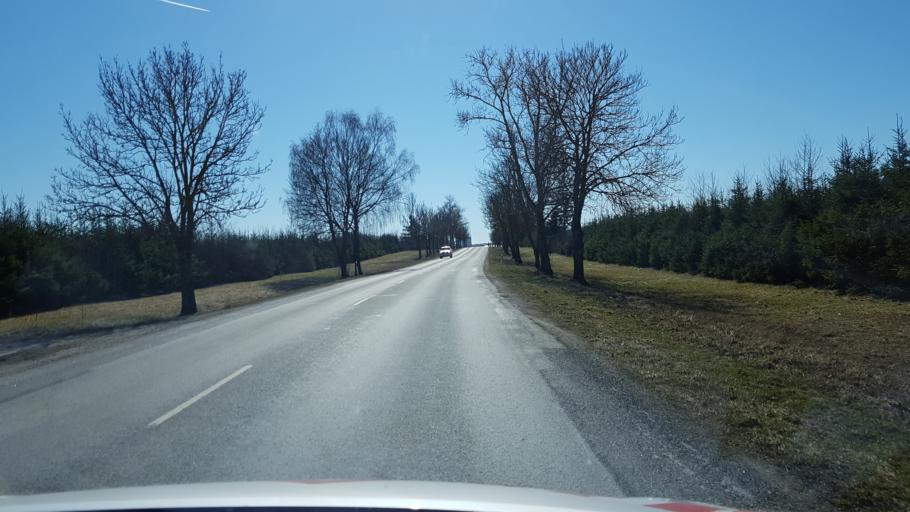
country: EE
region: Laeaene-Virumaa
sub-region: Rakvere linn
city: Rakvere
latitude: 59.3779
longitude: 26.3908
